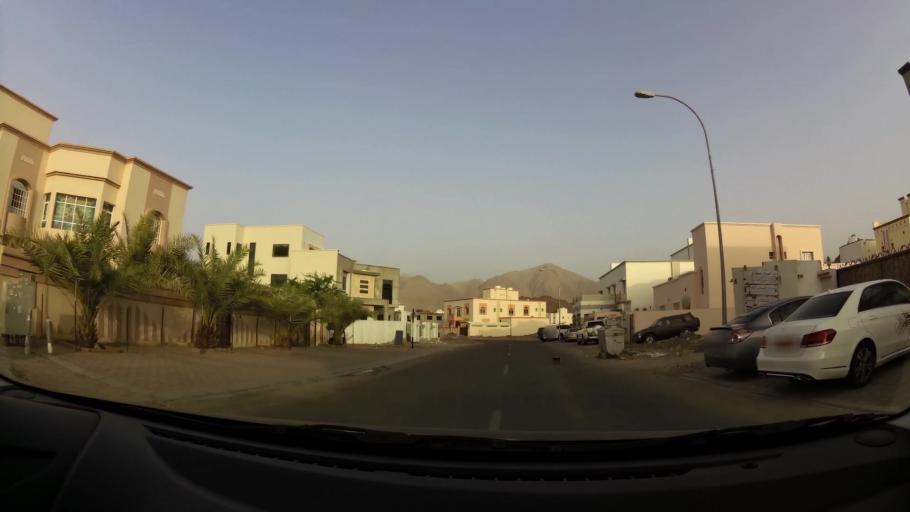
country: OM
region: Muhafazat Masqat
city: Bawshar
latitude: 23.5001
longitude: 58.3347
